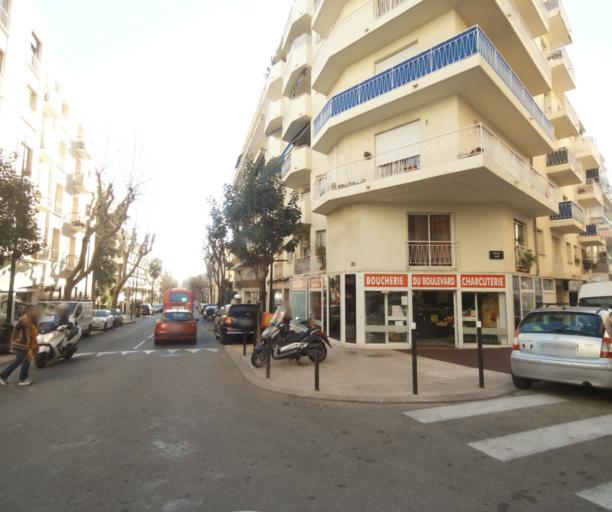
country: FR
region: Provence-Alpes-Cote d'Azur
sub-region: Departement des Alpes-Maritimes
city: Antibes
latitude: 43.5727
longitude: 7.1157
